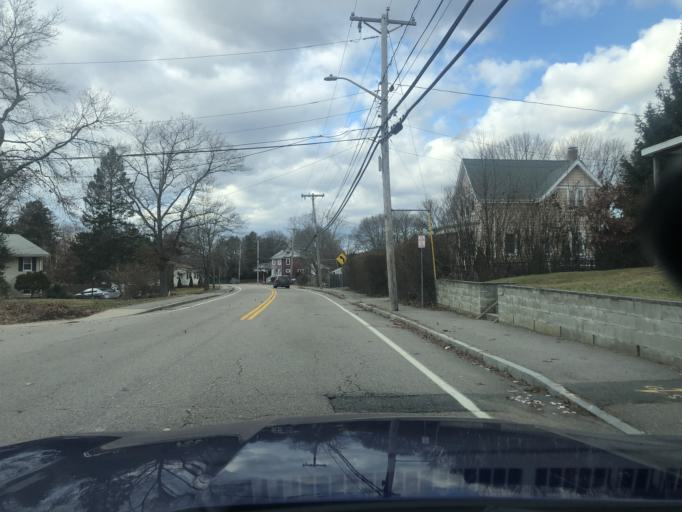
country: US
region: Massachusetts
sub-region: Plymouth County
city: Brockton
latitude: 42.1073
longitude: -71.0057
